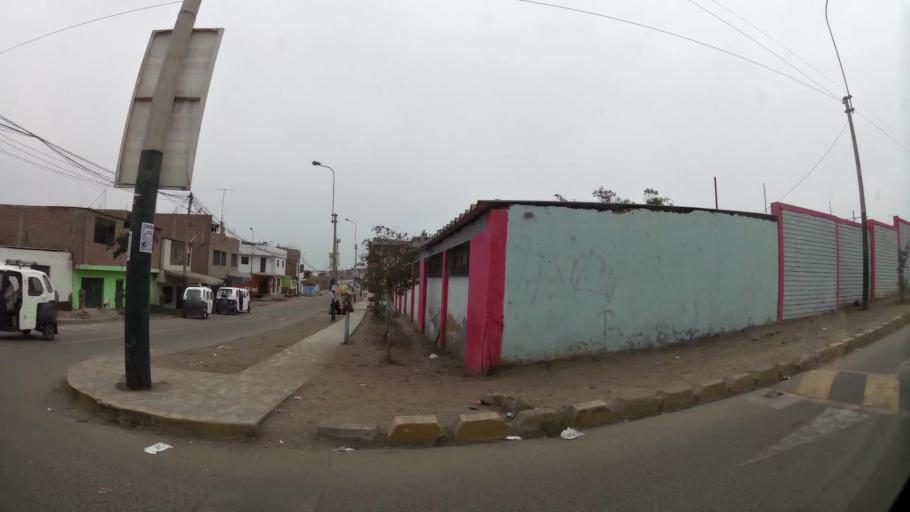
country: PE
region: Lima
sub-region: Lima
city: Surco
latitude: -12.1971
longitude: -76.9747
